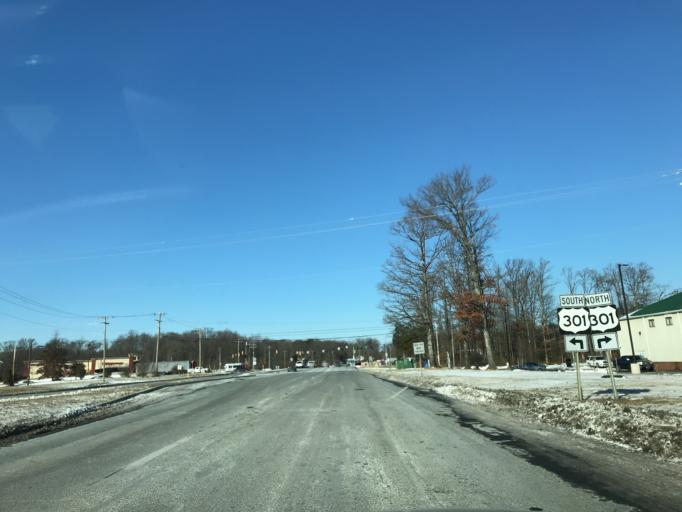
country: US
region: Maryland
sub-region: Charles County
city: Saint Charles
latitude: 38.5958
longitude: -76.9358
